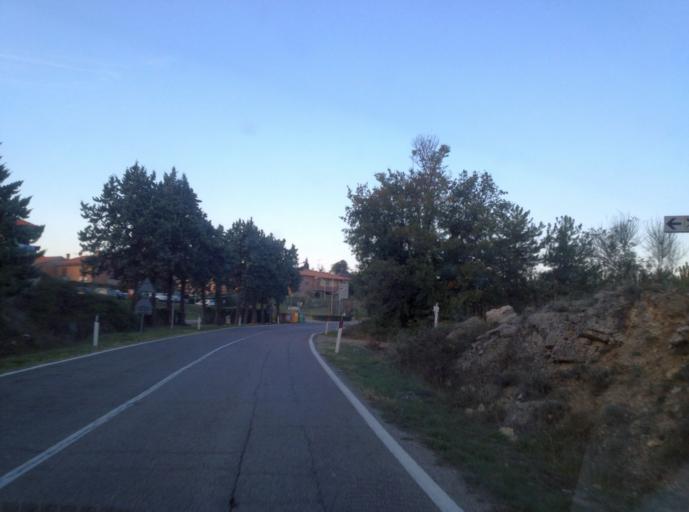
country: IT
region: Tuscany
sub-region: Provincia di Siena
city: Castellina in Chianti
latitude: 43.4541
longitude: 11.2922
